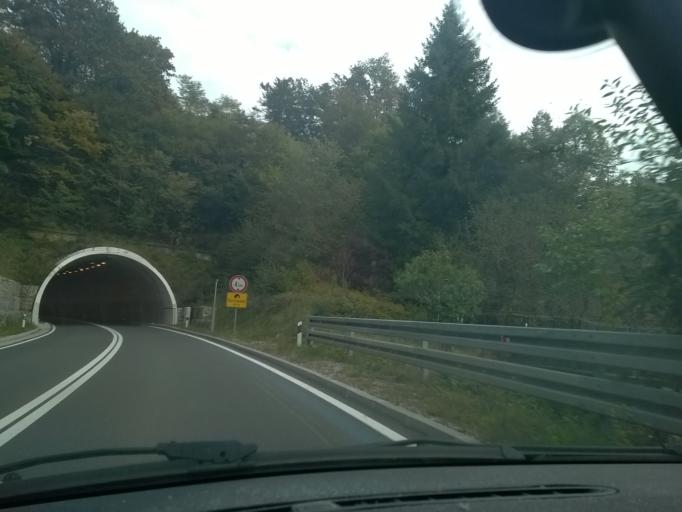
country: HR
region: Krapinsko-Zagorska
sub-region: Grad Krapina
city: Krapina
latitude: 46.2093
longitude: 15.8473
